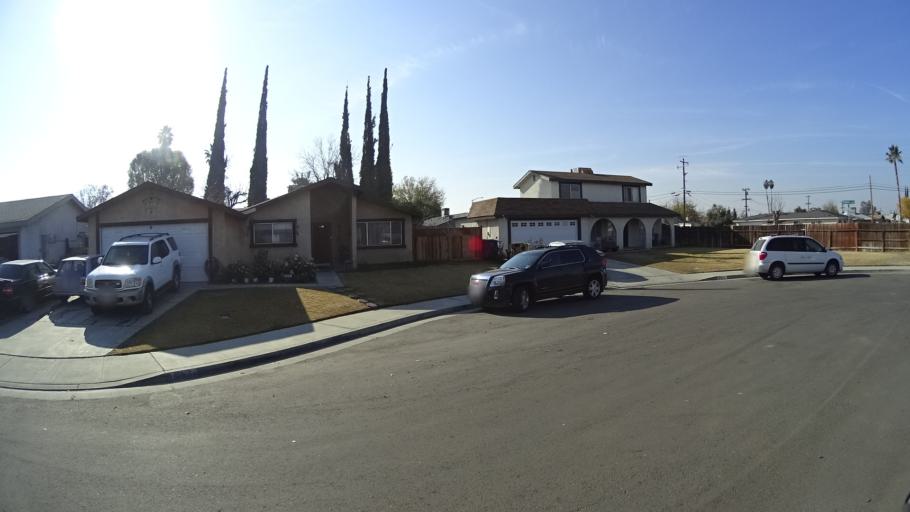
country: US
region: California
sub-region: Kern County
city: Greenfield
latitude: 35.3096
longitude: -119.0296
